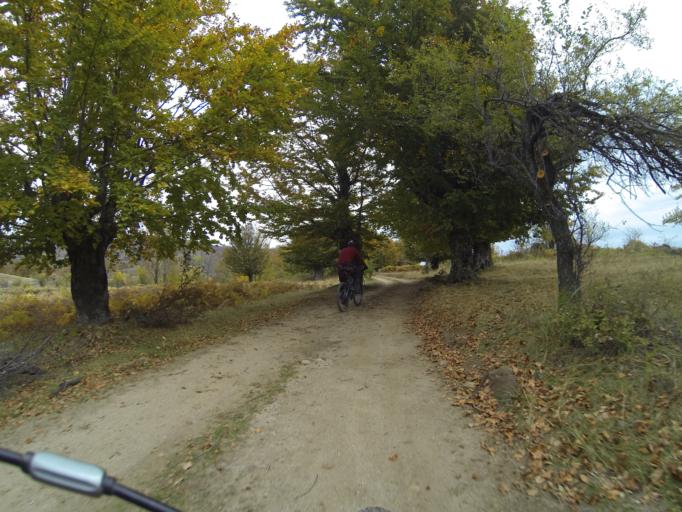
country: RO
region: Gorj
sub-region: Comuna Tismana
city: Sohodol
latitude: 45.1198
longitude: 22.8525
